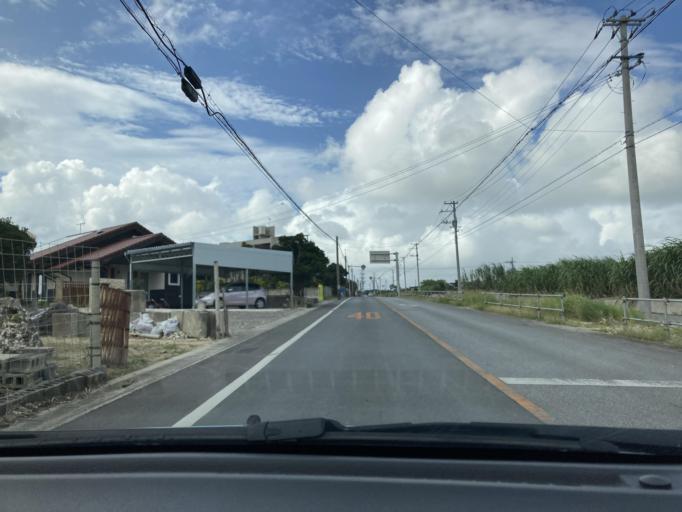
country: JP
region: Okinawa
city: Itoman
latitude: 26.1023
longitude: 127.6968
